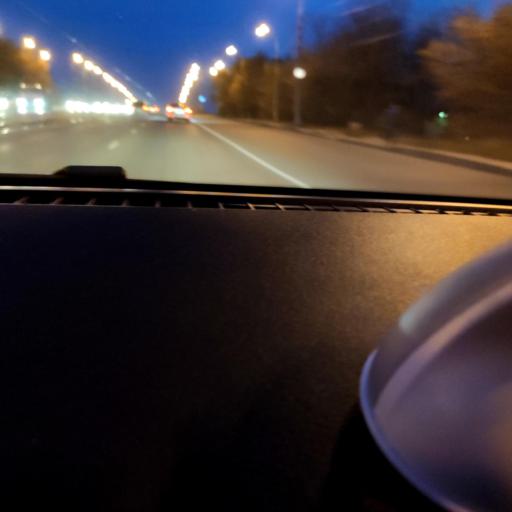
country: RU
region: Samara
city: Samara
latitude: 53.2151
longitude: 50.2680
